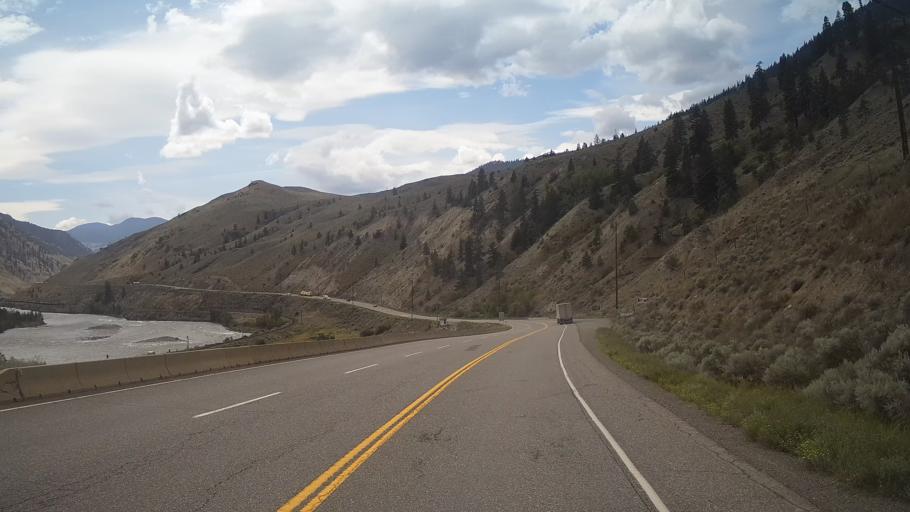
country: CA
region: British Columbia
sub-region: Thompson-Nicola Regional District
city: Ashcroft
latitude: 50.4860
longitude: -121.3001
